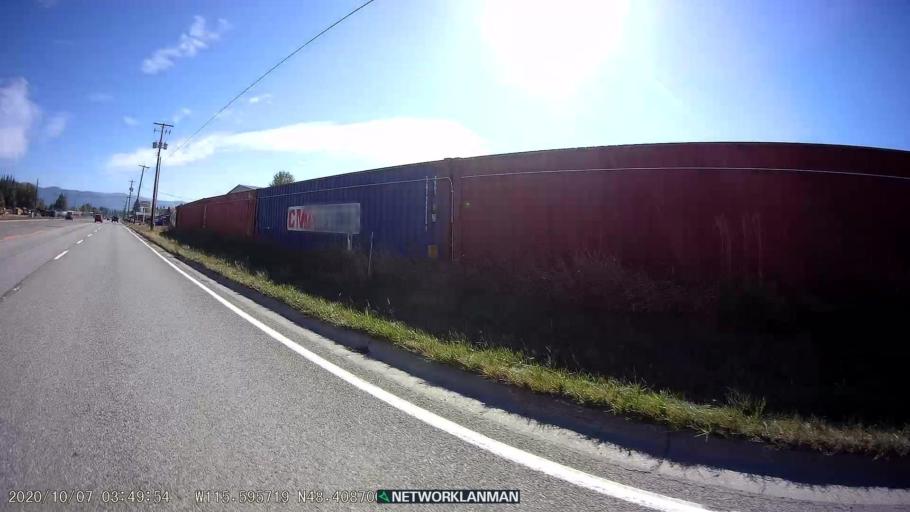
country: US
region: Montana
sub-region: Lincoln County
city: Libby
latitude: 48.4083
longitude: -115.5949
